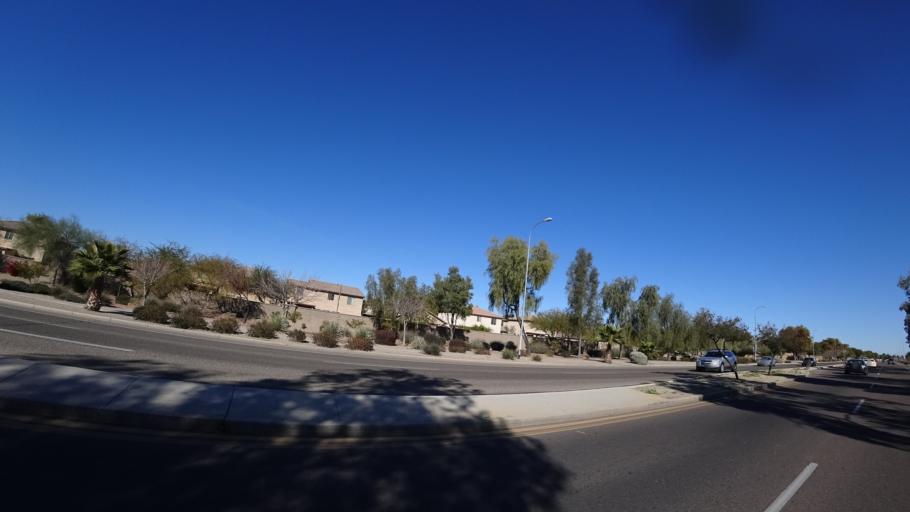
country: US
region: Arizona
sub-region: Maricopa County
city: Tolleson
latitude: 33.4218
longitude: -112.2486
